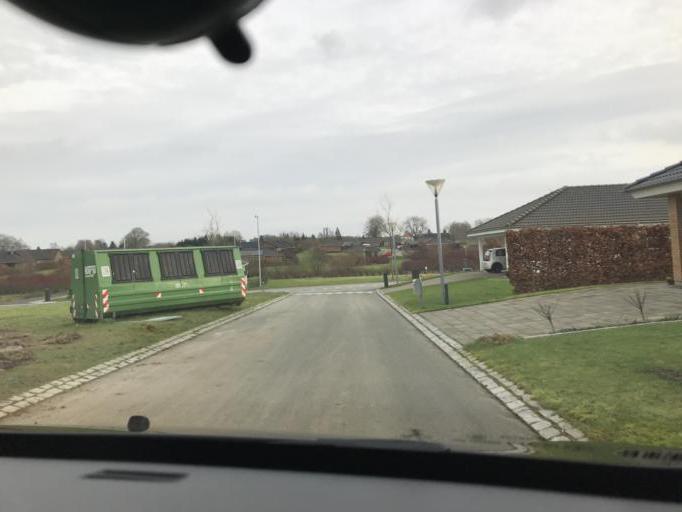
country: DK
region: South Denmark
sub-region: Faaborg-Midtfyn Kommune
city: Ringe
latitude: 55.2474
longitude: 10.4613
